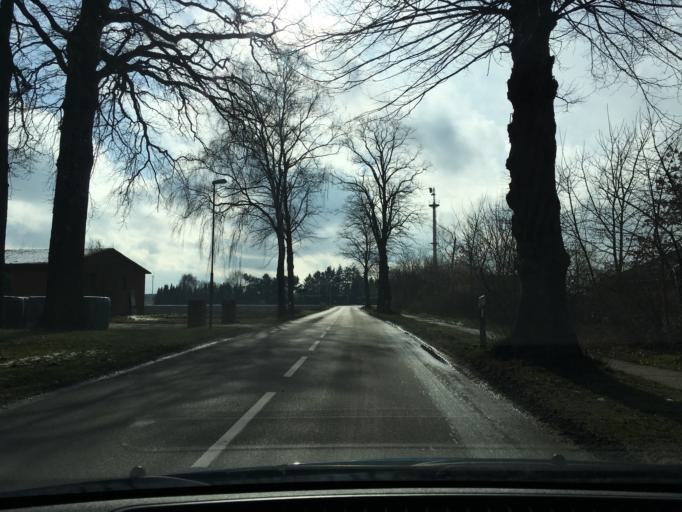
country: DE
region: Lower Saxony
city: Wittorf
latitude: 53.3314
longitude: 10.3794
